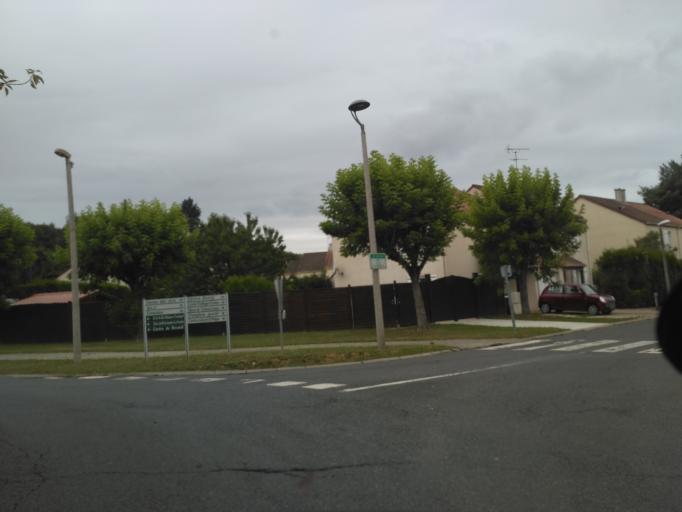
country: FR
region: Ile-de-France
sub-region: Departement de Seine-et-Marne
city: Vert-Saint-Denis
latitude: 48.5627
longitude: 2.6219
